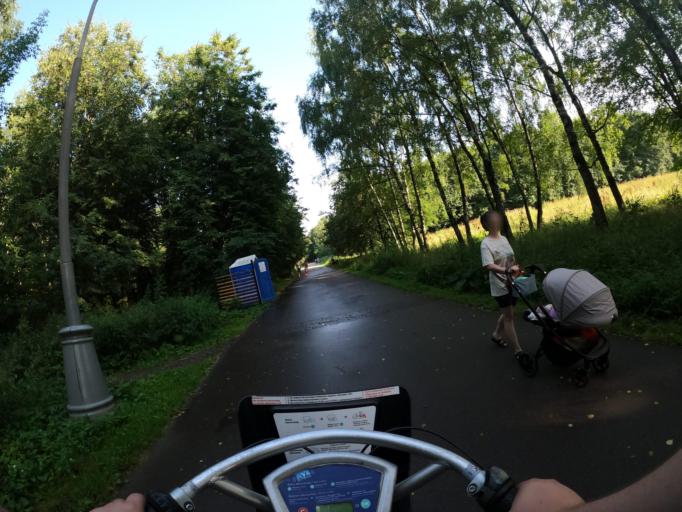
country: RU
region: Moscow
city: Strogino
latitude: 55.8208
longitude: 37.3986
